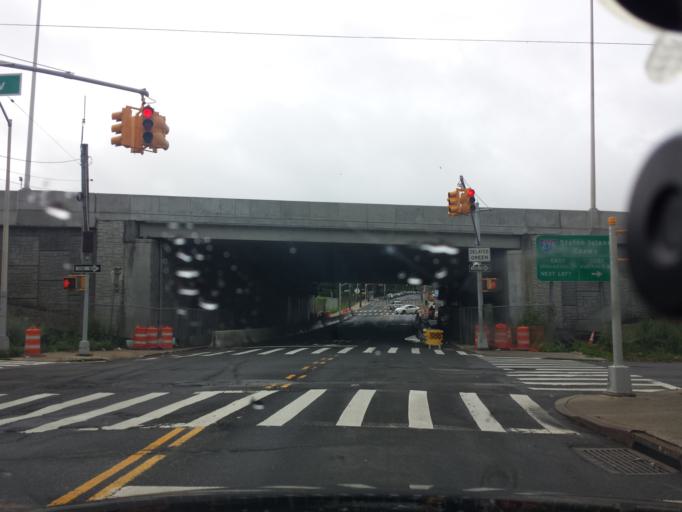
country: US
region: New York
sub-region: Richmond County
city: Staten Island
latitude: 40.6103
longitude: -74.1216
